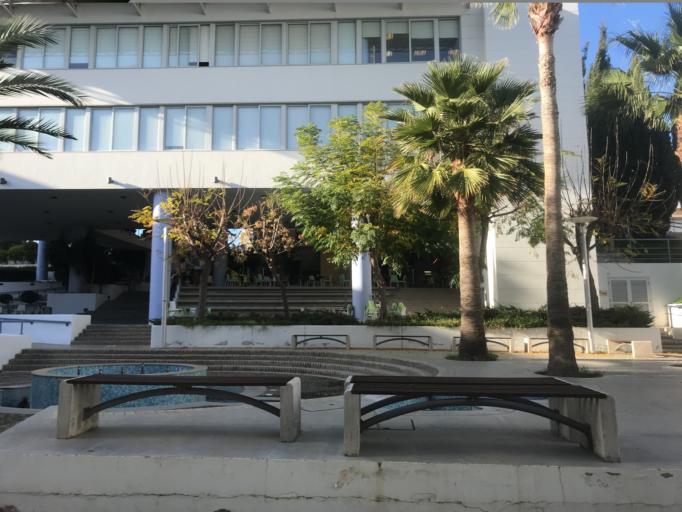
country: CY
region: Lefkosia
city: Geri
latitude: 35.1447
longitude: 33.4111
